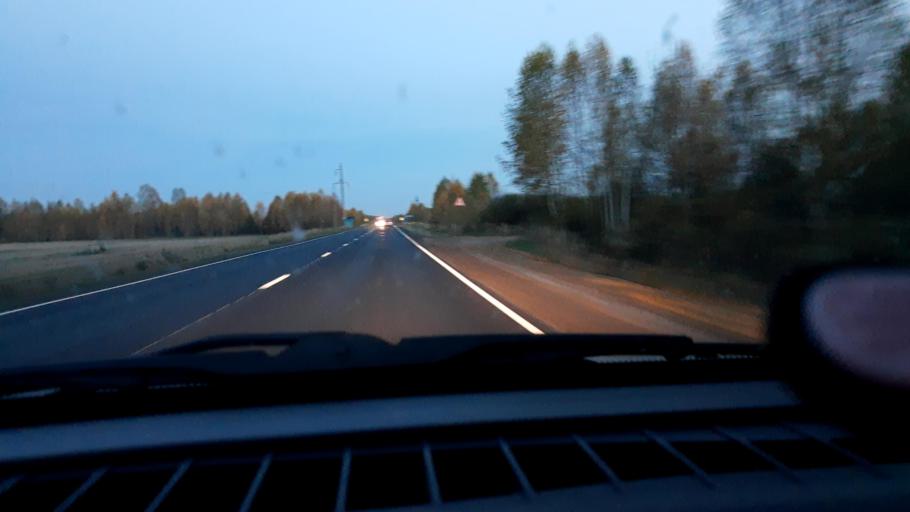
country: RU
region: Nizjnij Novgorod
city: Novaya Balakhna
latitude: 56.5887
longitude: 43.6666
